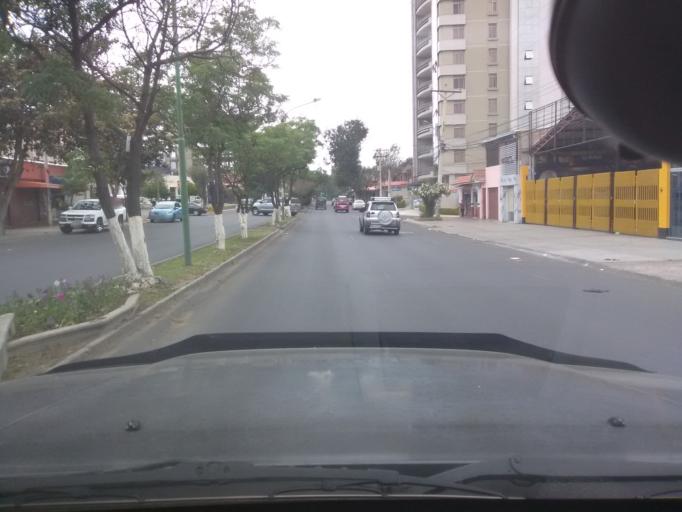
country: BO
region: Cochabamba
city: Cochabamba
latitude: -17.3718
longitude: -66.1741
